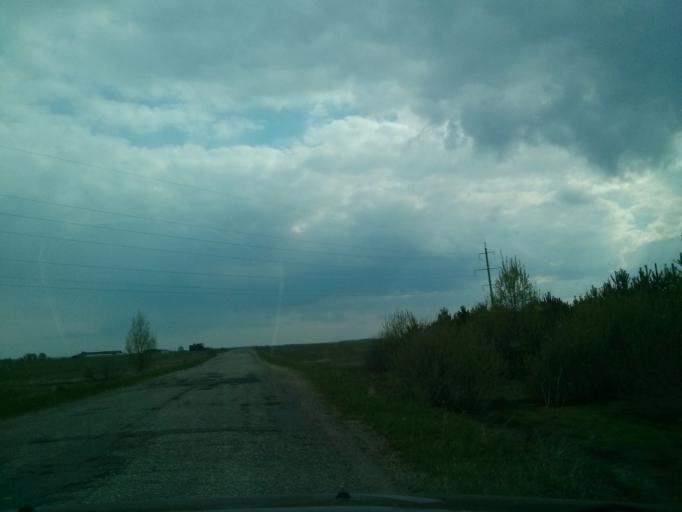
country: RU
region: Vladimir
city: Melenki
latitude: 55.3238
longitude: 41.7777
